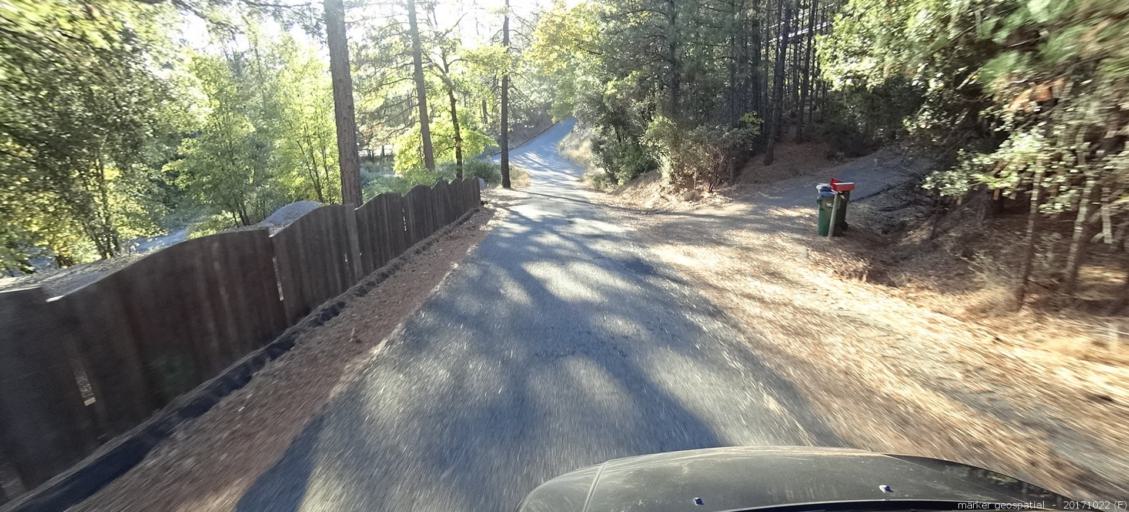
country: US
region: California
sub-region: Shasta County
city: Shasta Lake
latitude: 40.8522
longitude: -122.3344
